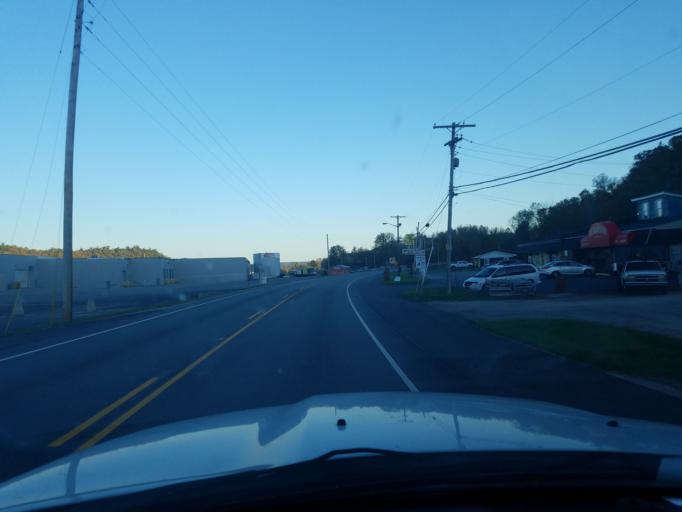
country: US
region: Indiana
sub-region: Washington County
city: New Pekin
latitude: 38.4647
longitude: -85.9408
